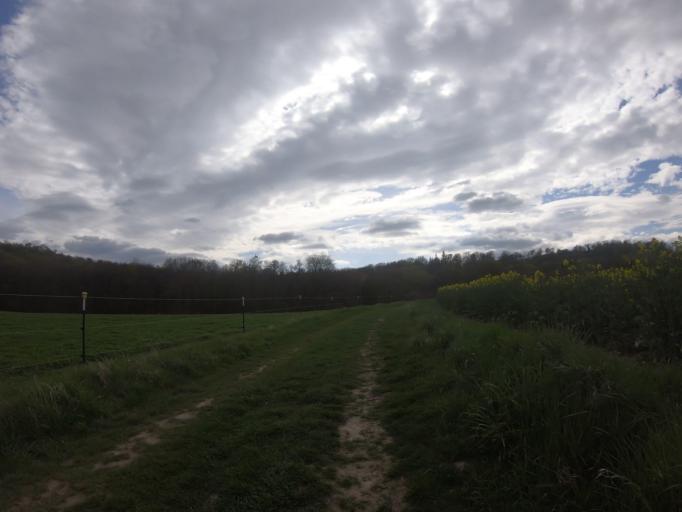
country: DE
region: Lower Saxony
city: Nordstemmen
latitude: 52.1777
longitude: 9.7722
